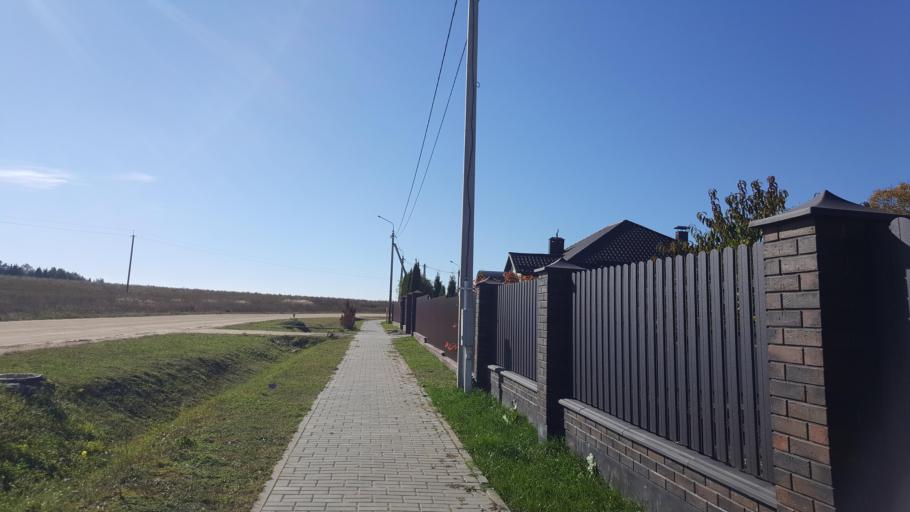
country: BY
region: Brest
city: Kamyanyets
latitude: 52.3867
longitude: 23.8109
